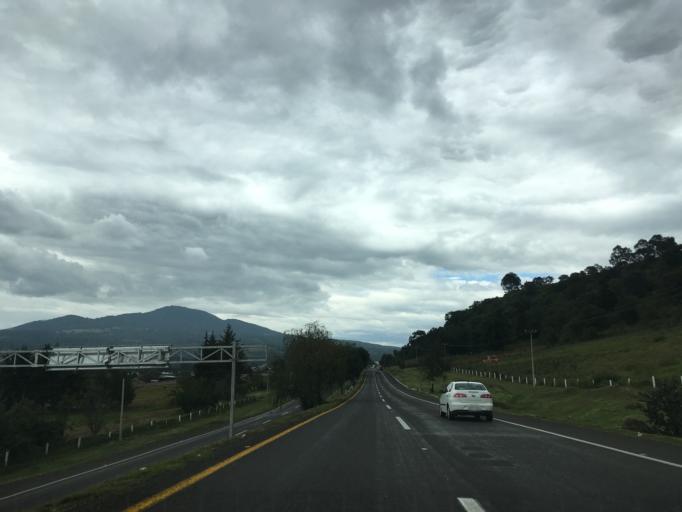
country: MX
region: Michoacan
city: Huiramba
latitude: 19.5529
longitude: -101.4297
